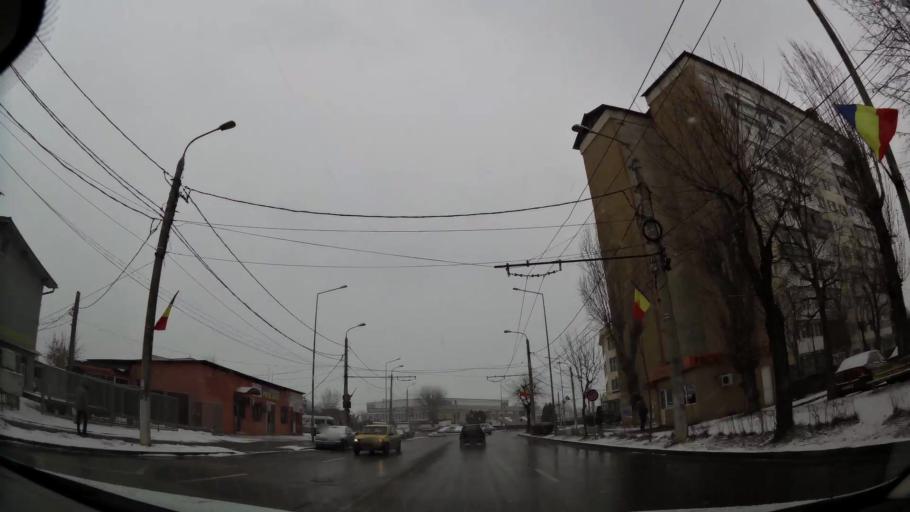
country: RO
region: Dambovita
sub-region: Municipiul Targoviste
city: Targoviste
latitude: 44.9263
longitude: 25.4397
